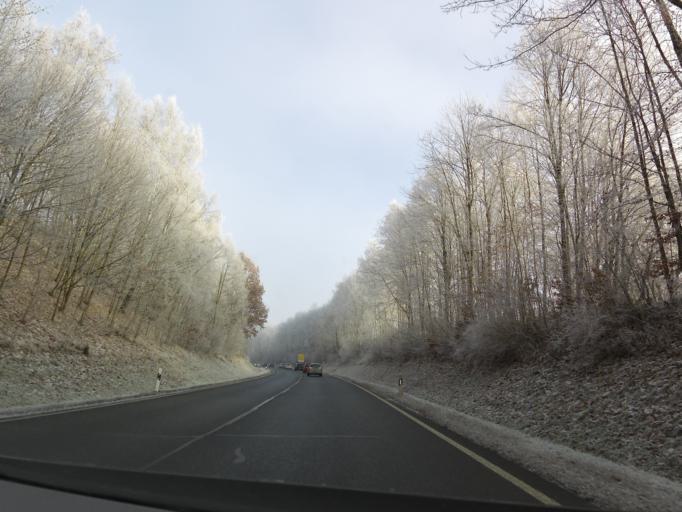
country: DE
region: Bavaria
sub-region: Upper Franconia
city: Arzberg
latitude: 50.0615
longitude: 12.1809
